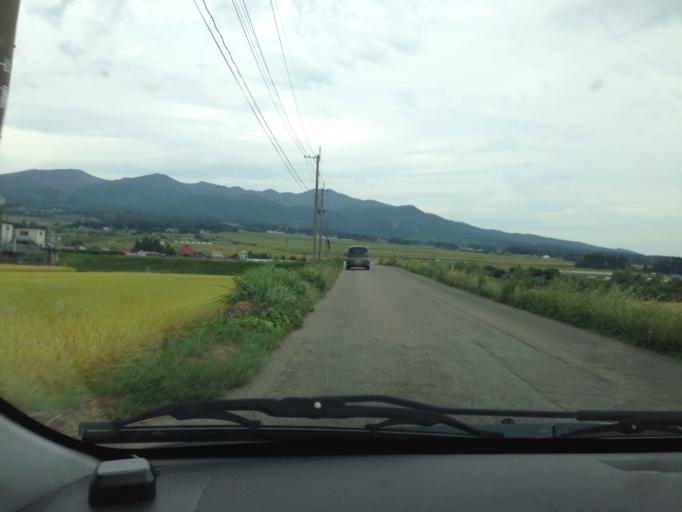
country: JP
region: Fukushima
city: Kitakata
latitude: 37.6321
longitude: 139.9154
